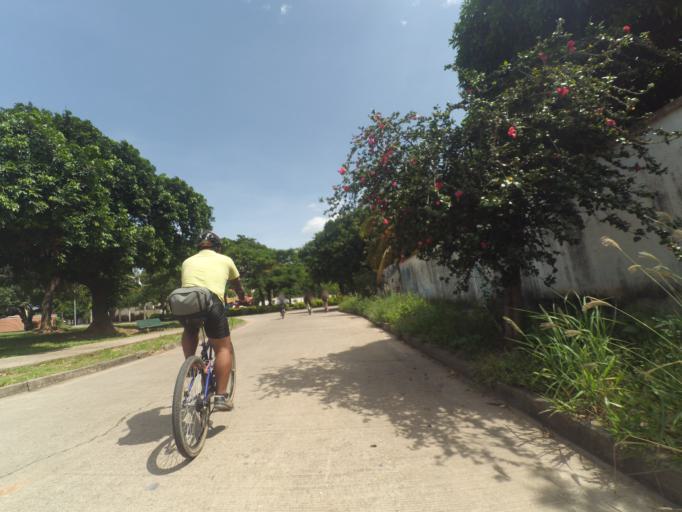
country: BO
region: Santa Cruz
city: Santa Cruz de la Sierra
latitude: -17.7671
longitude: -63.1742
